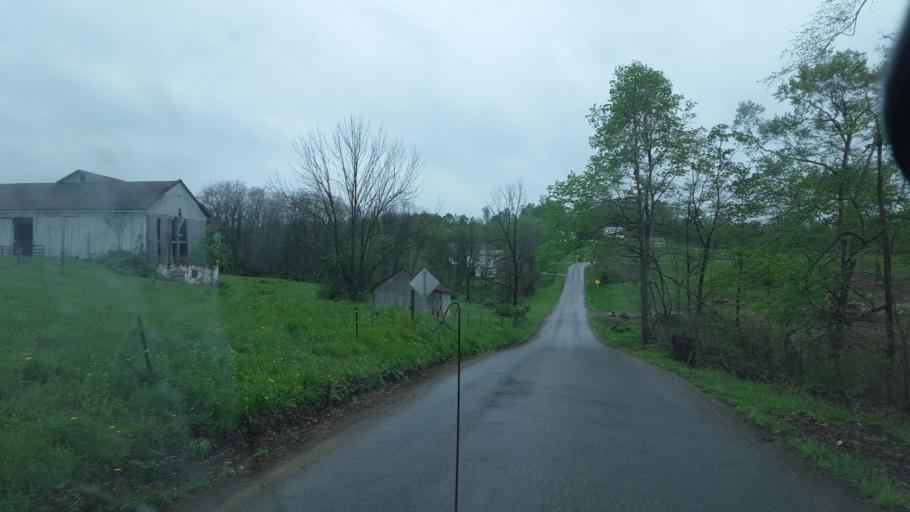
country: US
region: Ohio
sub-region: Holmes County
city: Millersburg
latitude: 40.6106
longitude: -81.8716
